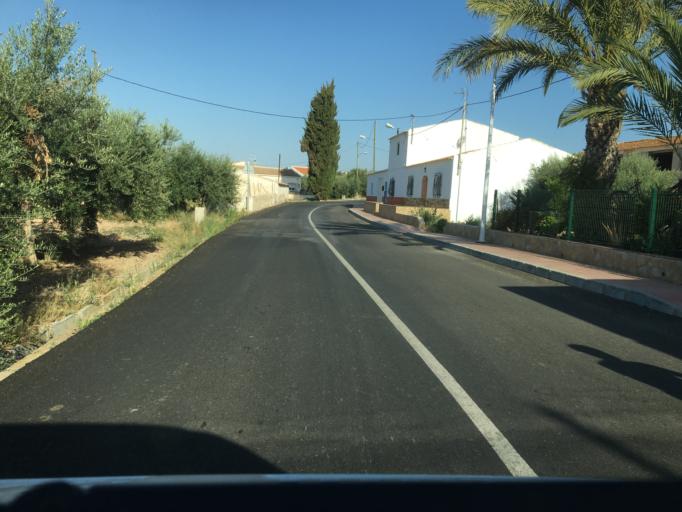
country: ES
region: Andalusia
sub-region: Provincia de Almeria
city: Huercal-Overa
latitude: 37.4692
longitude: -1.8922
